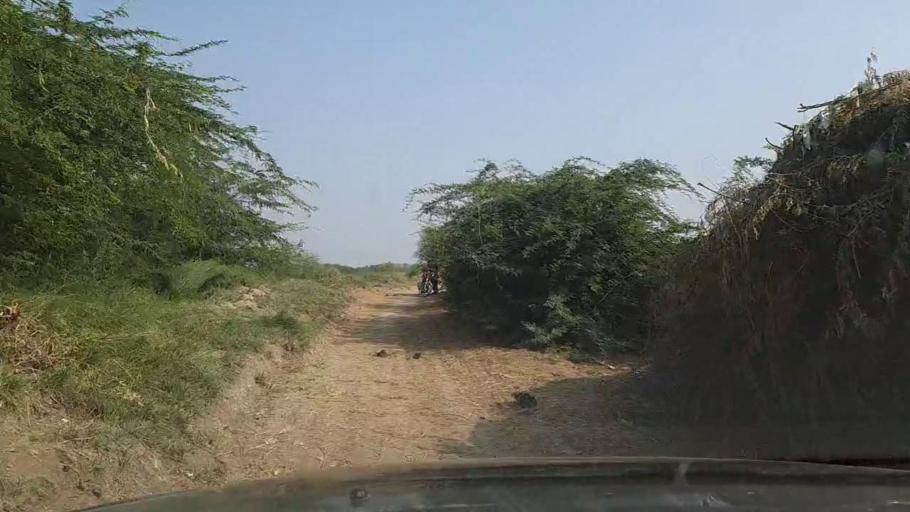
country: PK
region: Sindh
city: Mirpur Batoro
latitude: 24.6809
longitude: 68.2370
